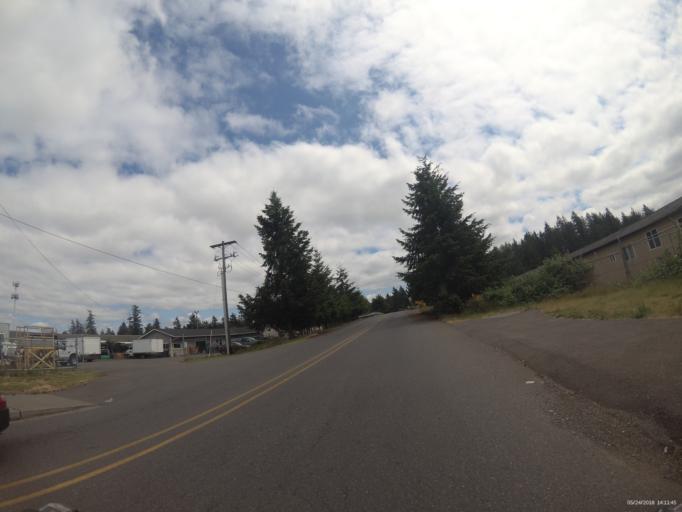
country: US
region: Washington
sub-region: Pierce County
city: McChord Air Force Base
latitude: 47.1424
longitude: -122.5158
